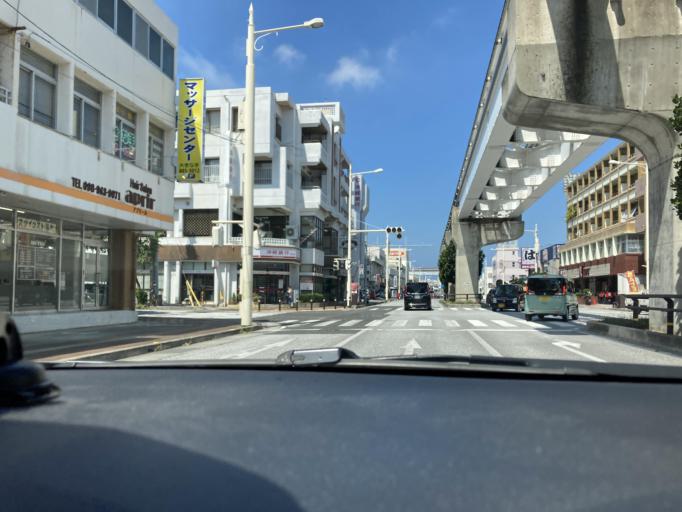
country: JP
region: Okinawa
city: Naha-shi
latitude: 26.2300
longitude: 127.7065
